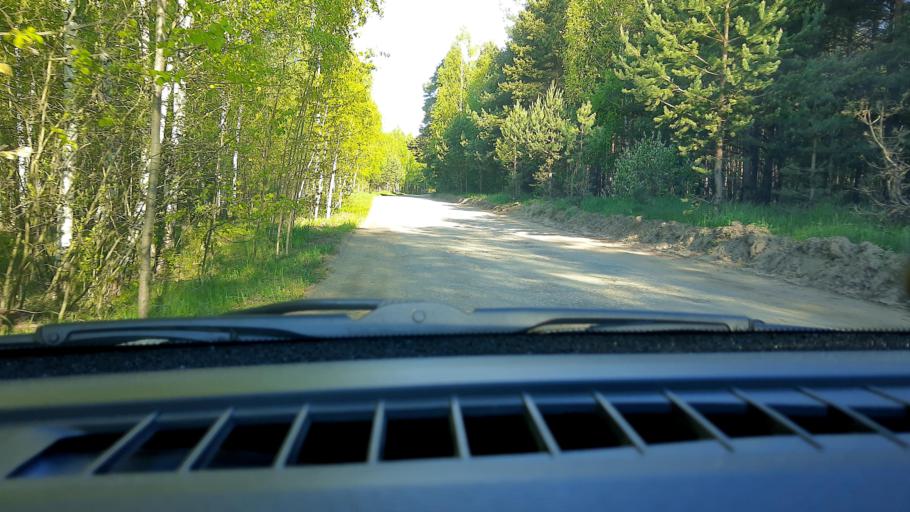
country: RU
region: Nizjnij Novgorod
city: Sitniki
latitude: 56.4139
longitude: 44.0554
